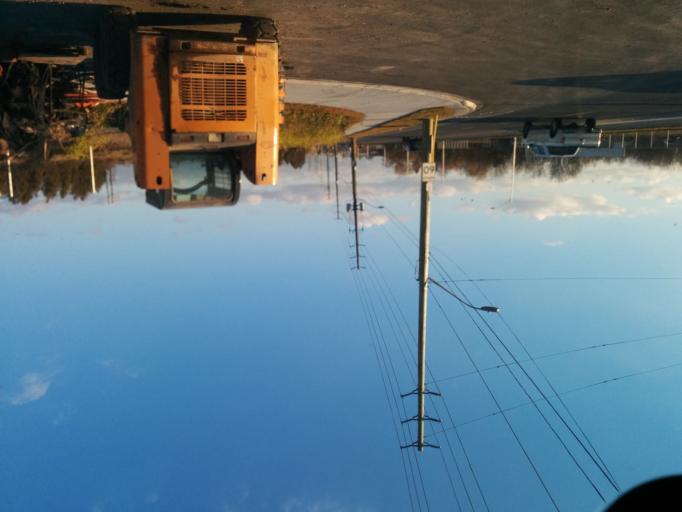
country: CA
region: Ontario
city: Oakville
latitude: 43.5019
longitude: -79.6884
